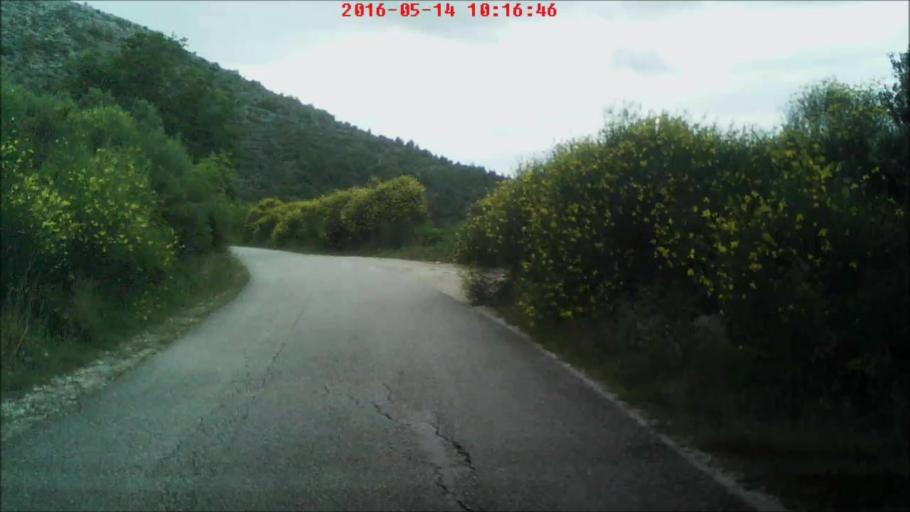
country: HR
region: Dubrovacko-Neretvanska
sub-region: Grad Dubrovnik
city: Mokosica
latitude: 42.7242
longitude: 17.9646
